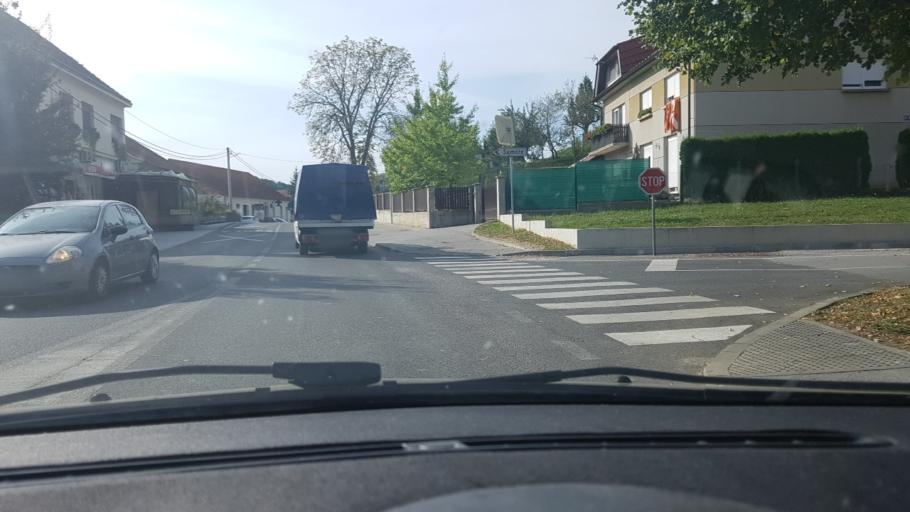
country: HR
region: Krapinsko-Zagorska
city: Zlatar
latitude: 46.0935
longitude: 16.0428
